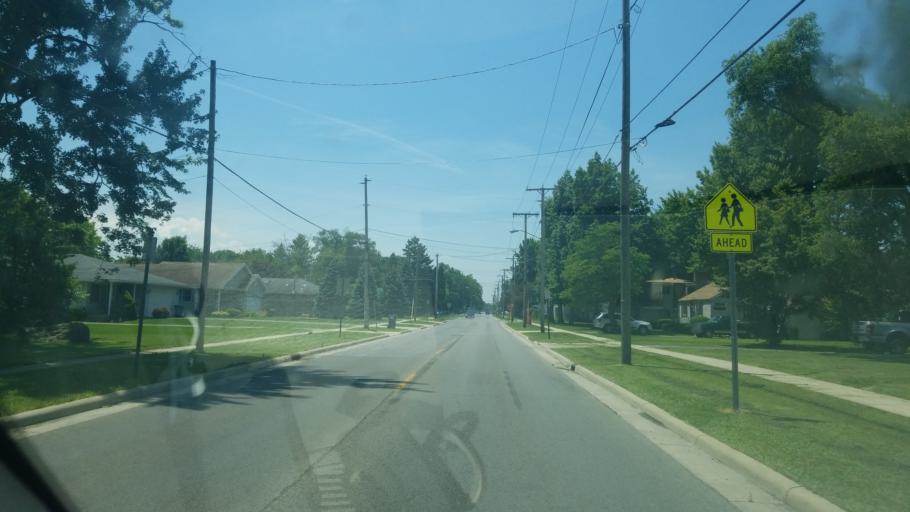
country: US
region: Ohio
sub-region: Hancock County
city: Findlay
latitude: 41.0588
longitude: -83.6374
